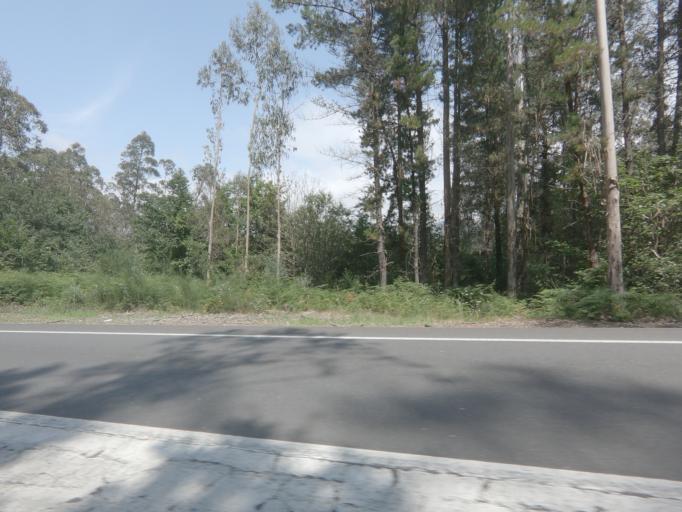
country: ES
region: Galicia
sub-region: Provincia de Pontevedra
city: Gondomar
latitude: 42.0818
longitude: -8.7506
